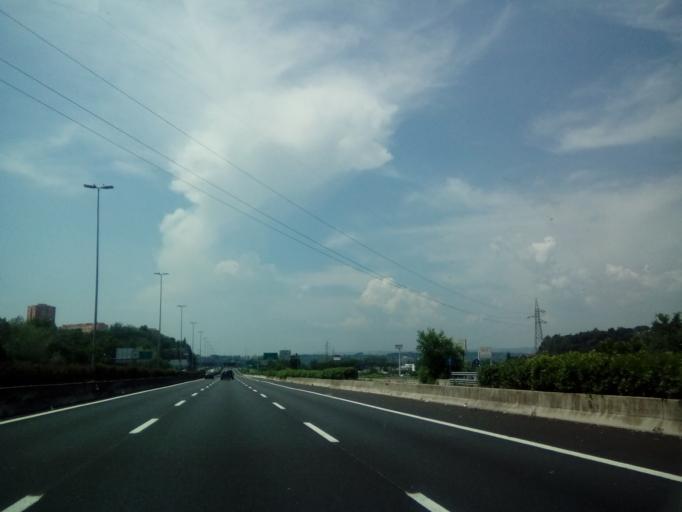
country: IT
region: Latium
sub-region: Citta metropolitana di Roma Capitale
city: Rome
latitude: 41.9843
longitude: 12.5237
